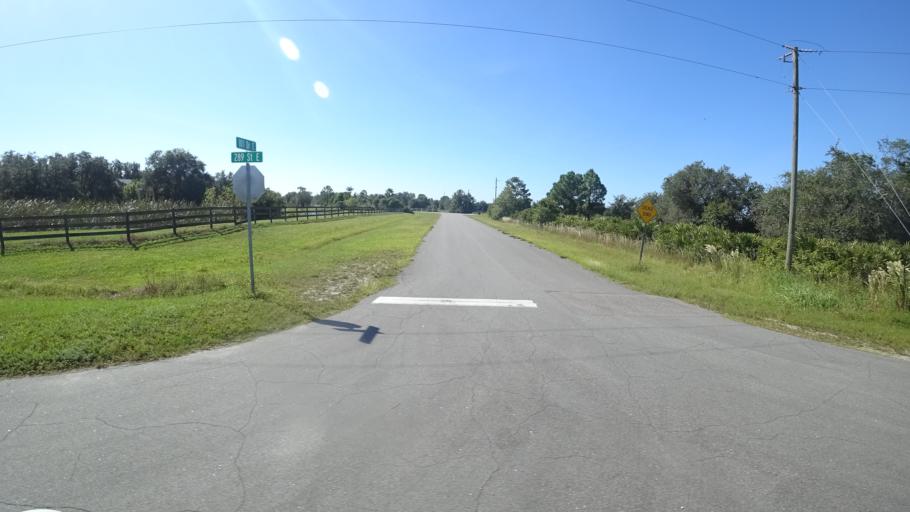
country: US
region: Florida
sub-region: Sarasota County
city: Lake Sarasota
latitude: 27.3595
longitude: -82.2454
